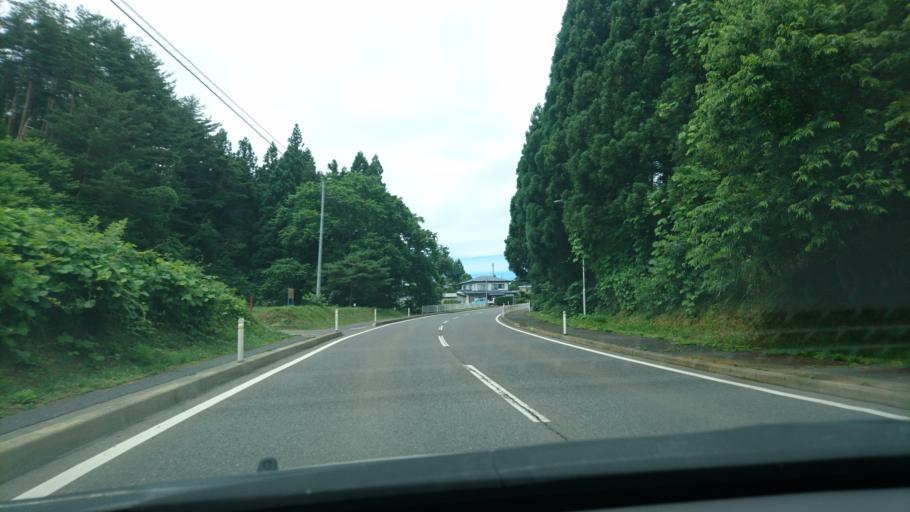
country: JP
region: Iwate
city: Miyako
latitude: 39.9173
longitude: 141.9025
